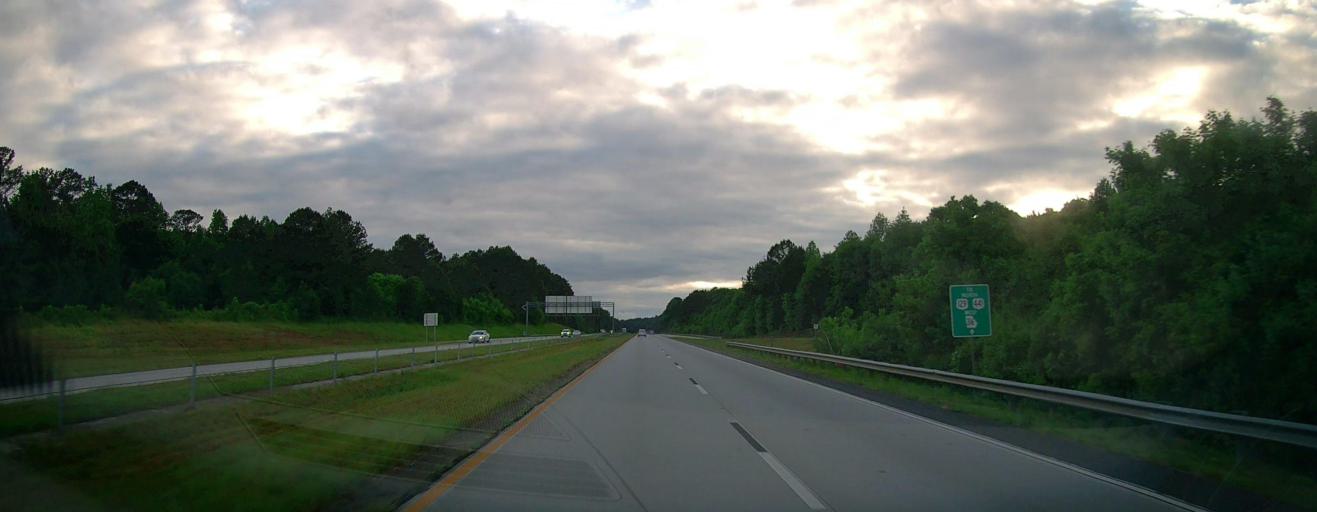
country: US
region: Georgia
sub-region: Oconee County
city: Watkinsville
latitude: 33.9163
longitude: -83.4086
